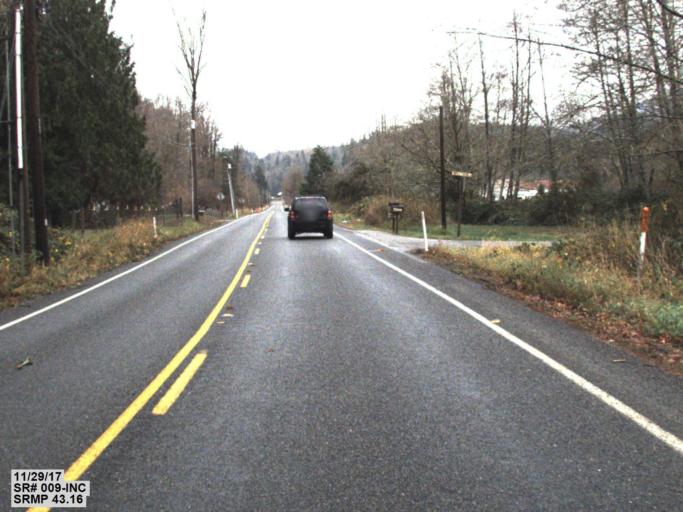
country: US
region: Washington
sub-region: Skagit County
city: Big Lake
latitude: 48.3481
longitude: -122.2031
